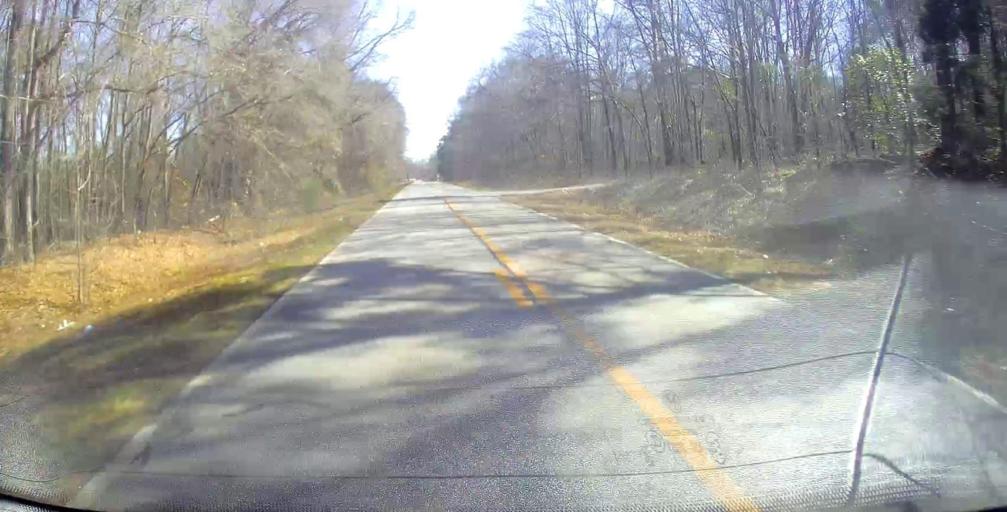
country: US
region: Georgia
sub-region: Peach County
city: Byron
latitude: 32.6048
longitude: -83.8007
